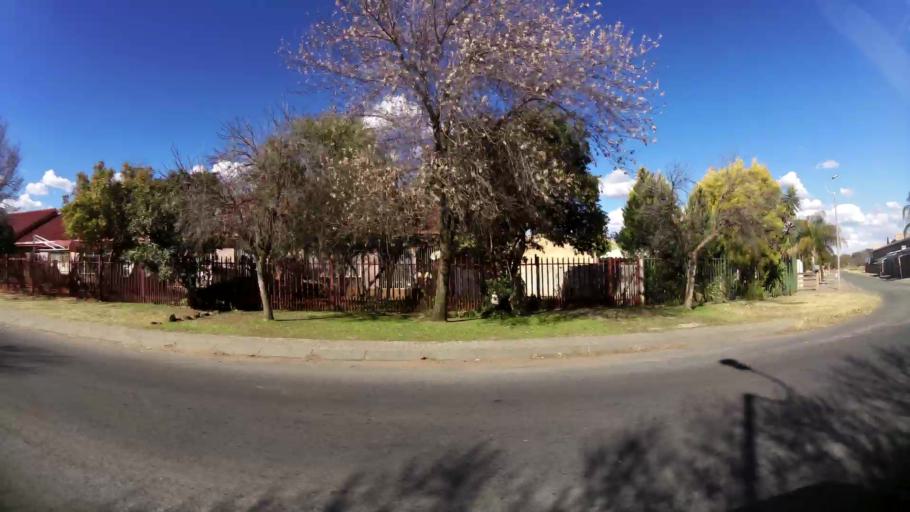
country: ZA
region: North-West
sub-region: Dr Kenneth Kaunda District Municipality
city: Klerksdorp
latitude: -26.8360
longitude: 26.6556
